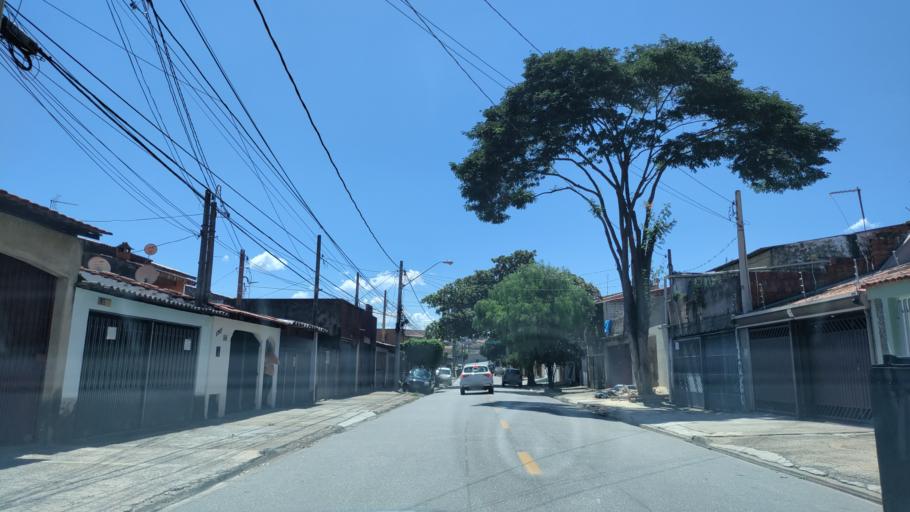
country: BR
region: Sao Paulo
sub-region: Sorocaba
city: Sorocaba
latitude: -23.4673
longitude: -47.4796
